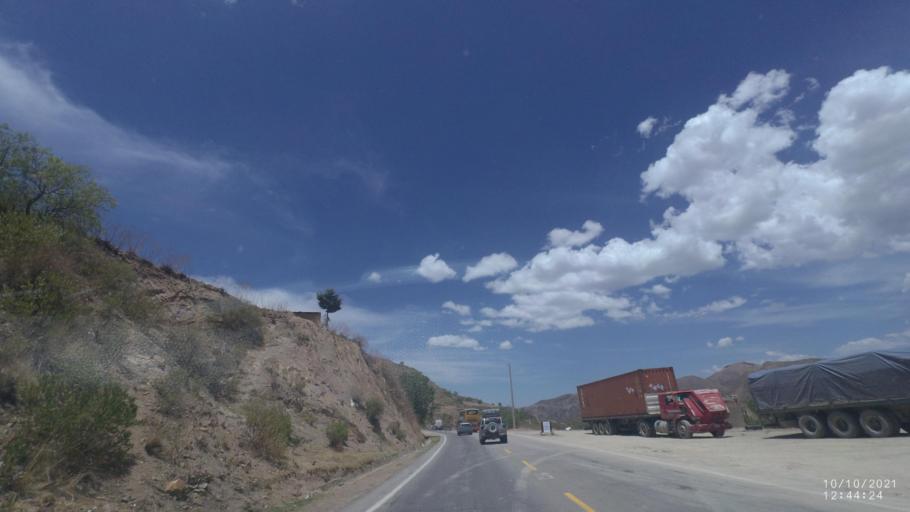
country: BO
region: Cochabamba
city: Irpa Irpa
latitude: -17.6310
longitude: -66.3764
